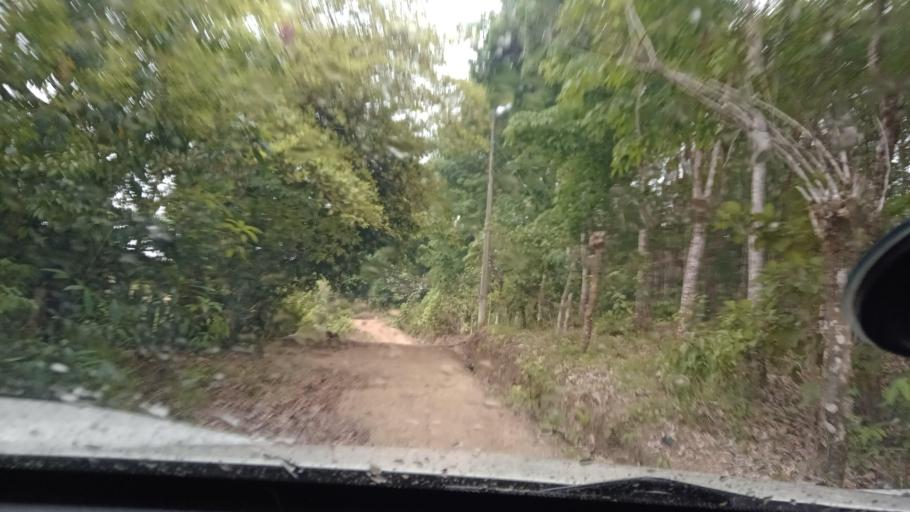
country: MX
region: Veracruz
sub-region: Uxpanapa
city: Poblado 10
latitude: 17.4491
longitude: -94.0885
